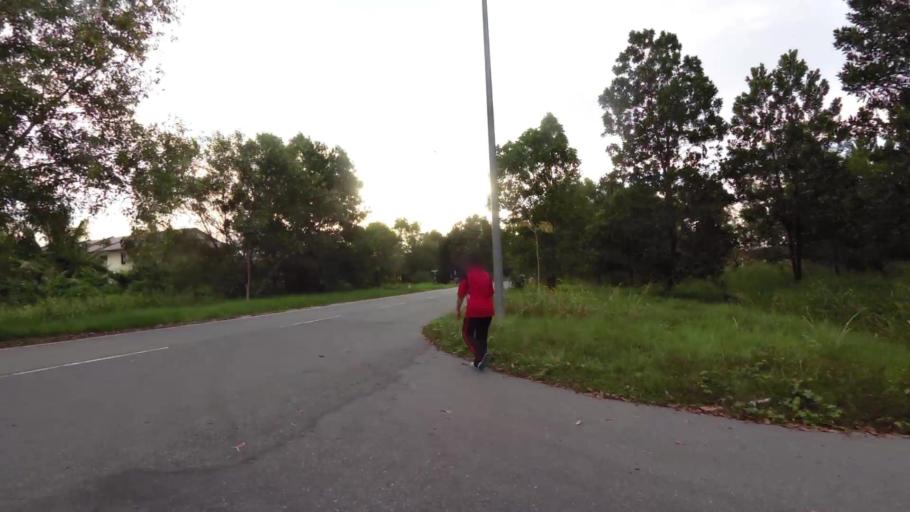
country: BN
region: Brunei and Muara
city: Bandar Seri Begawan
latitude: 4.9939
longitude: 114.9897
